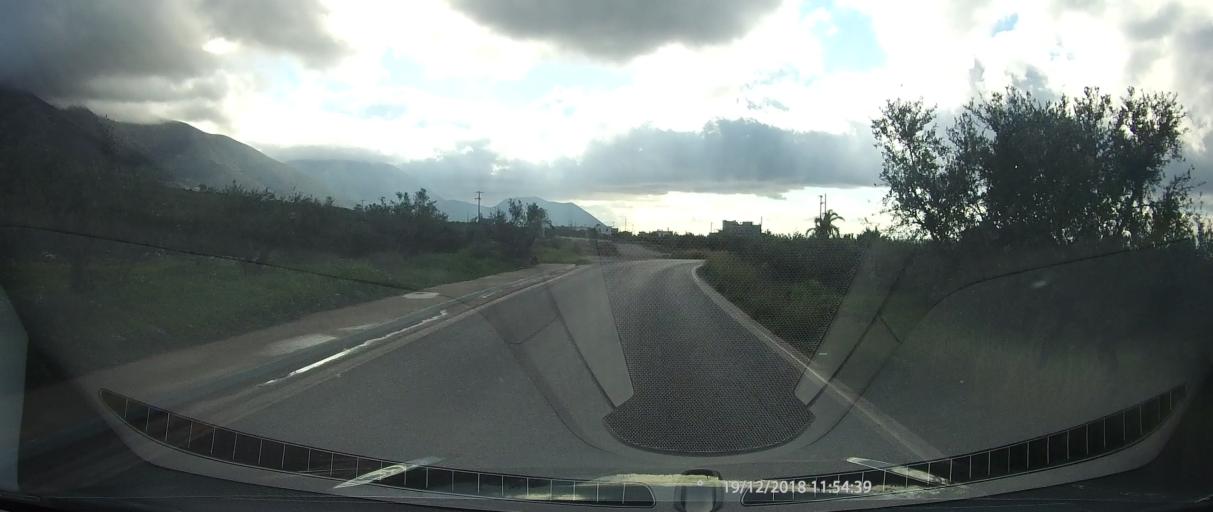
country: GR
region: Peloponnese
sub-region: Nomos Lakonias
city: Gytheio
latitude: 36.6155
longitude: 22.3911
